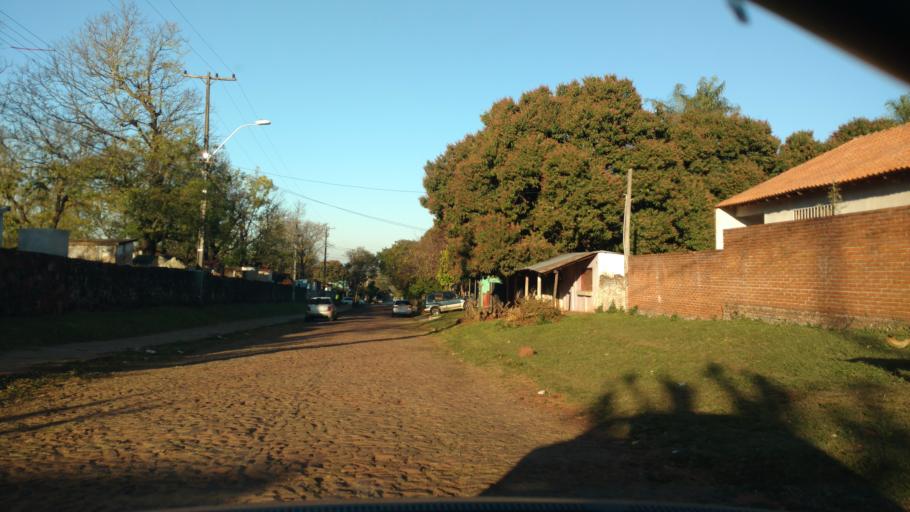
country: PY
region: Paraguari
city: Yaguaron
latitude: -25.5637
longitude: -57.2908
